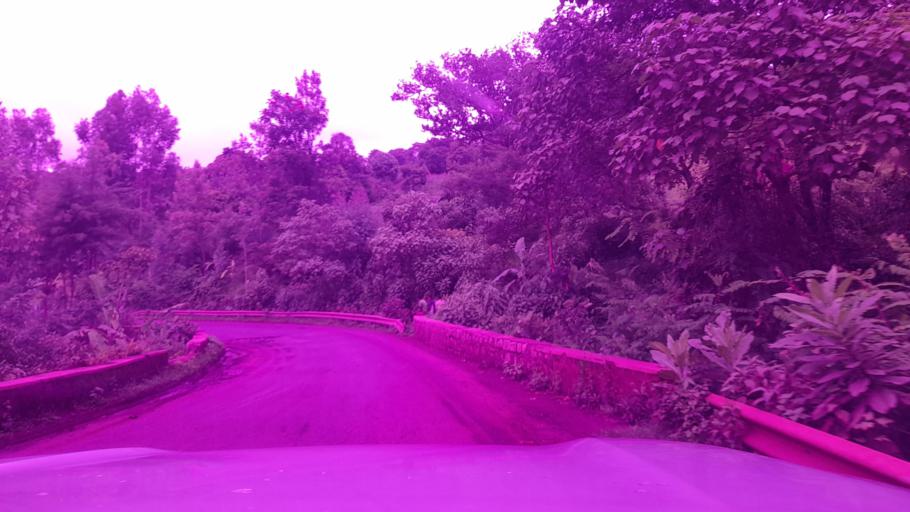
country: ET
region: Oromiya
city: Jima
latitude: 7.9110
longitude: 37.3979
